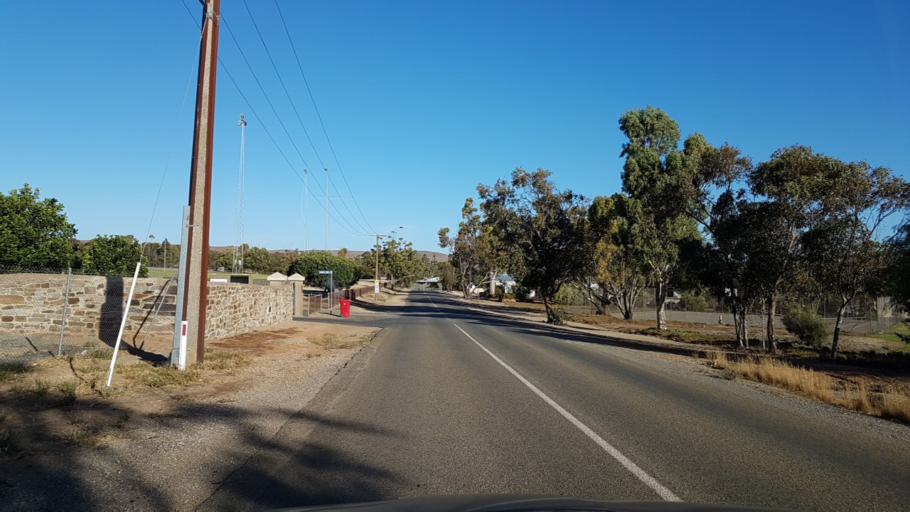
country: AU
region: South Australia
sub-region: Clare and Gilbert Valleys
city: Clare
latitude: -33.6758
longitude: 138.9397
